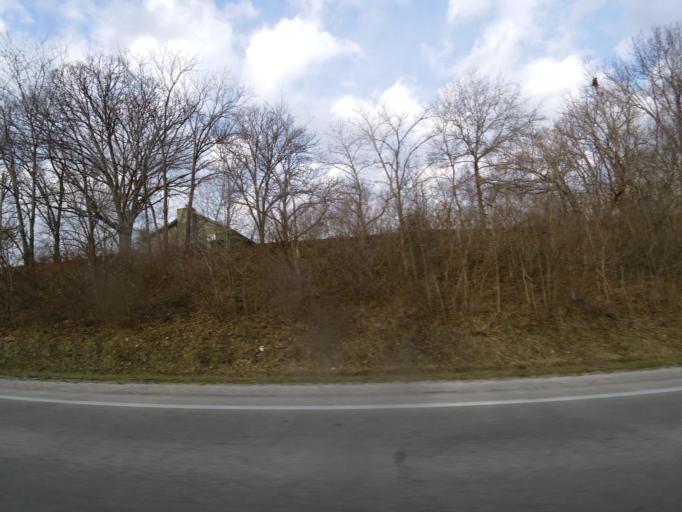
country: US
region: Illinois
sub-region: Christian County
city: Pana
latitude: 39.3024
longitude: -89.0873
